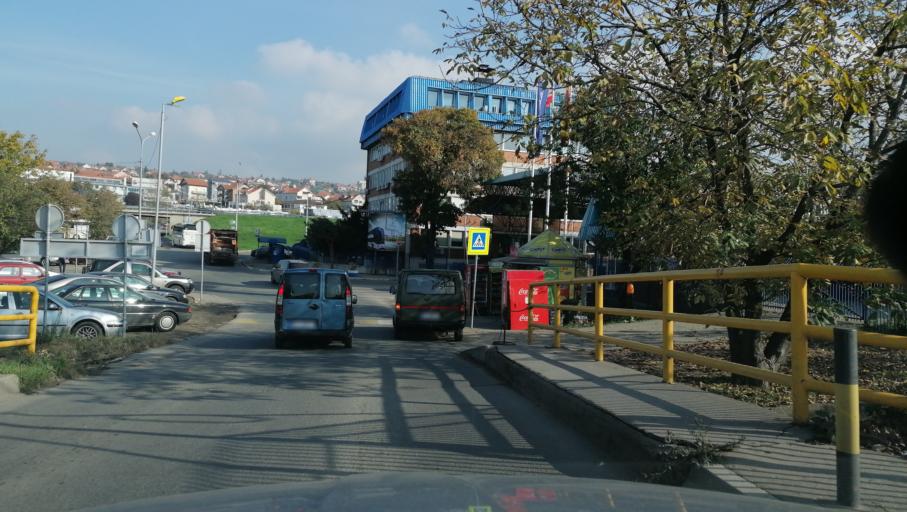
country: RS
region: Central Serbia
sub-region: Belgrade
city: Zvezdara
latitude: 44.7714
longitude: 20.5176
